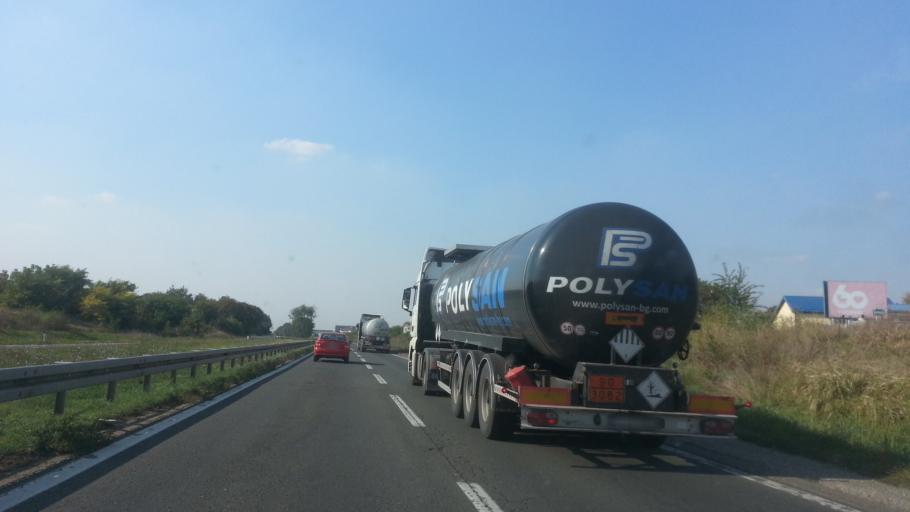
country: RS
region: Central Serbia
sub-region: Belgrade
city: Zemun
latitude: 44.8755
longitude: 20.3291
